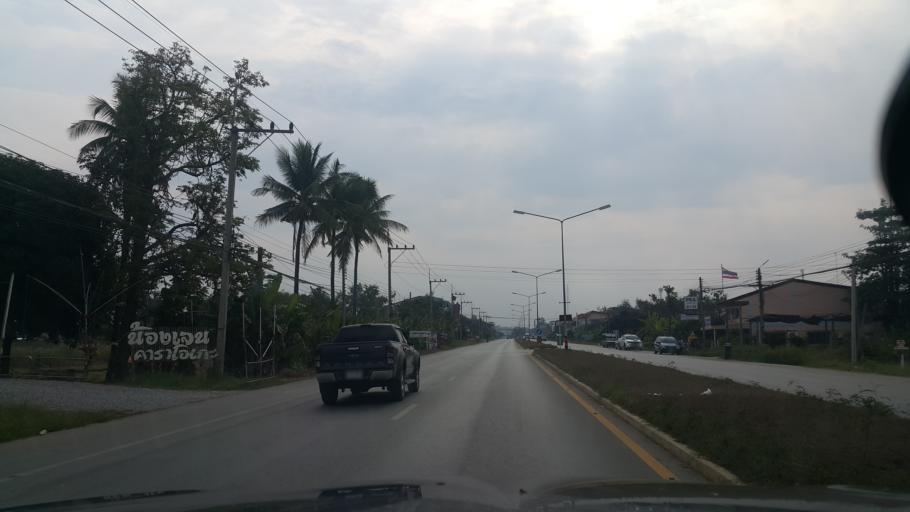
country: TH
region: Sukhothai
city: Si Samrong
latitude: 17.1744
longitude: 99.8534
